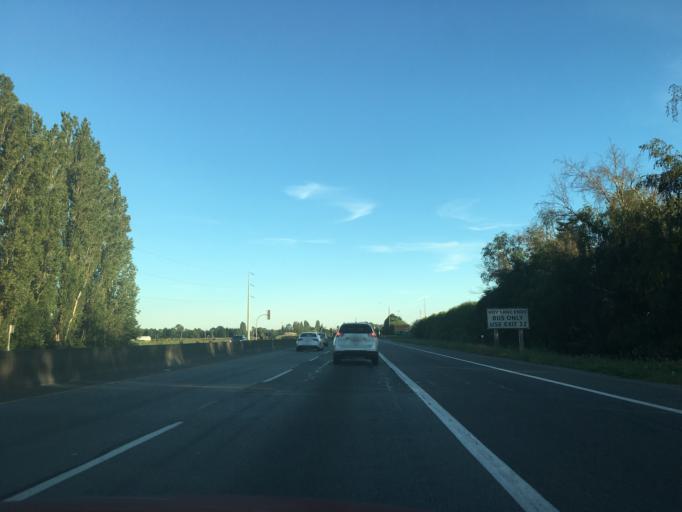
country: CA
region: British Columbia
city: Ladner
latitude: 49.1416
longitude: -123.0869
